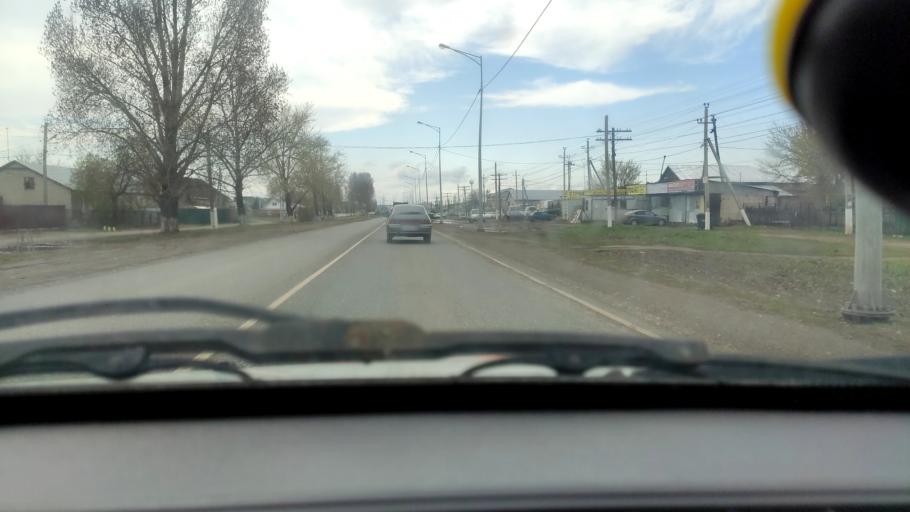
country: RU
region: Samara
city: Zhigulevsk
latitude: 53.5531
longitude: 49.5297
